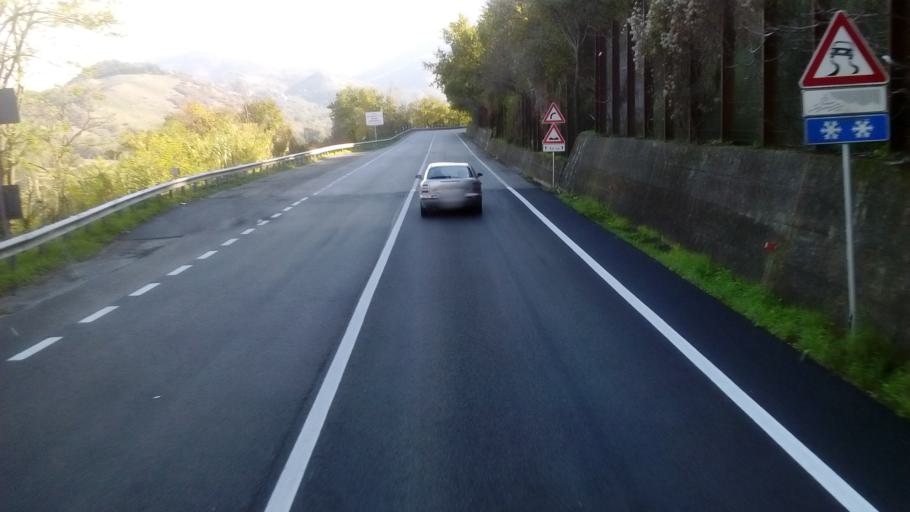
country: IT
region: Molise
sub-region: Provincia di Isernia
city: Conca Casale
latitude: 41.4566
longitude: 14.0133
